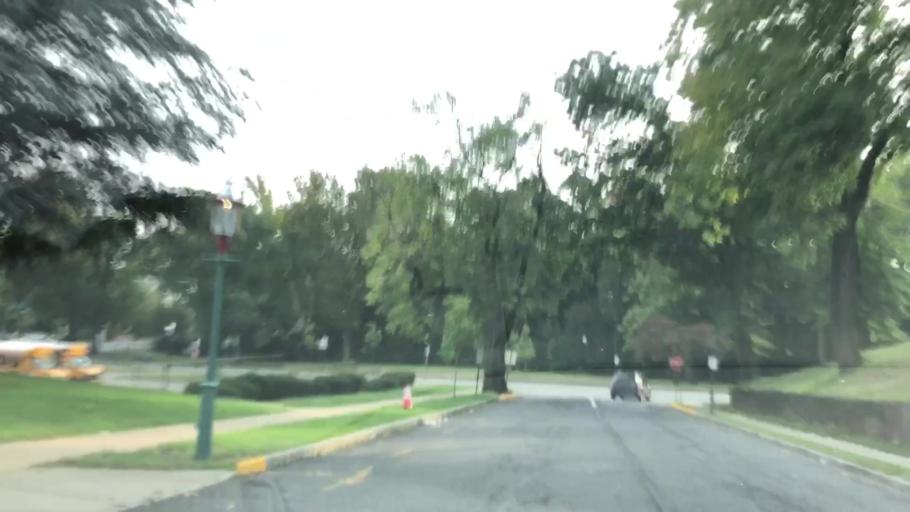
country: US
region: New Jersey
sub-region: Essex County
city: Glen Ridge
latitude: 40.8003
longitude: -74.2023
